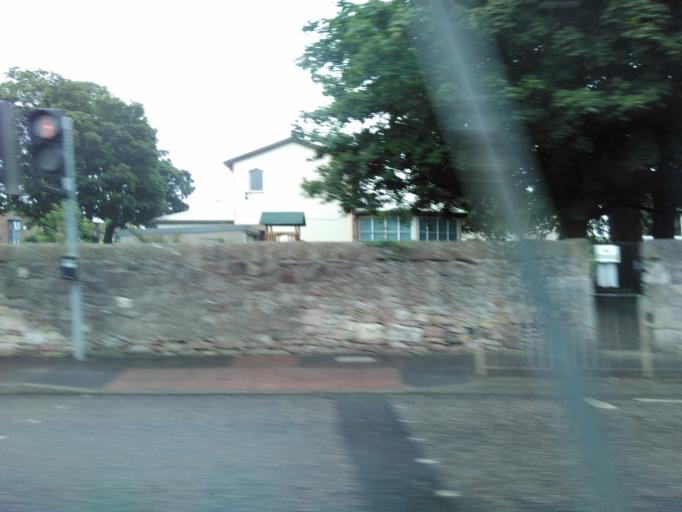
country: GB
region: Scotland
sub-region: Midlothian
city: Loanhead
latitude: 55.9224
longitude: -3.1628
